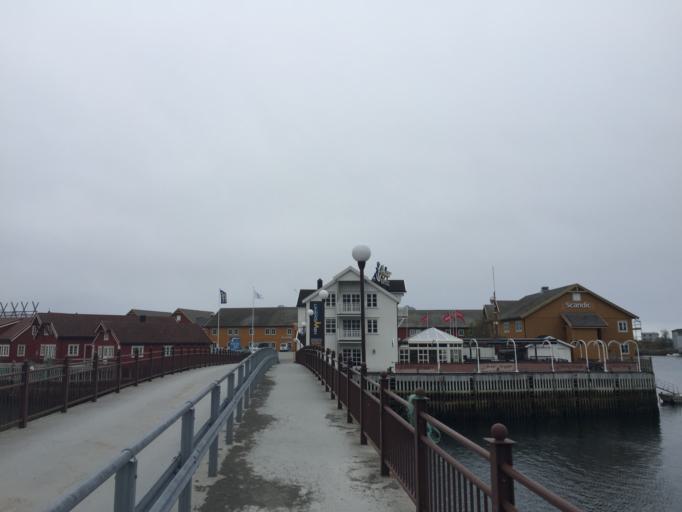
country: NO
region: Nordland
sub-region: Vagan
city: Svolvaer
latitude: 68.2335
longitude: 14.5685
